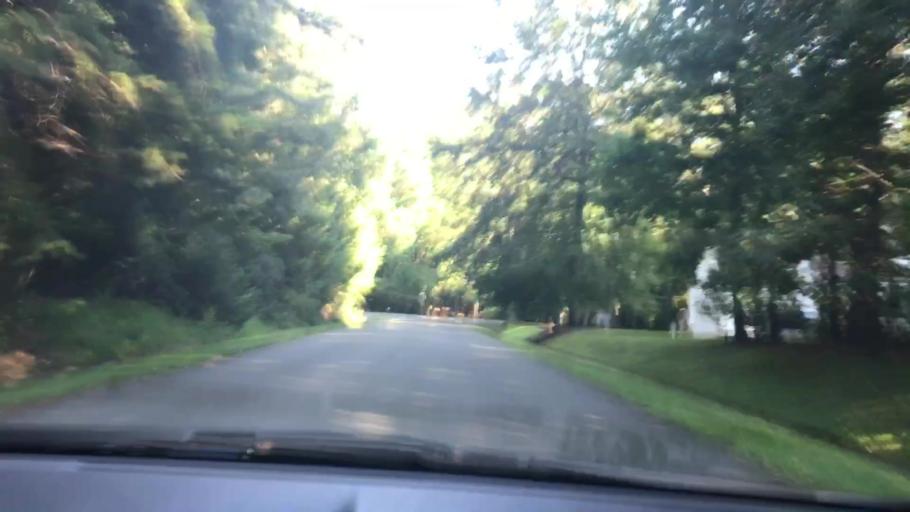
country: US
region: Virginia
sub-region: Henrico County
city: Short Pump
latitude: 37.6089
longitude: -77.7162
